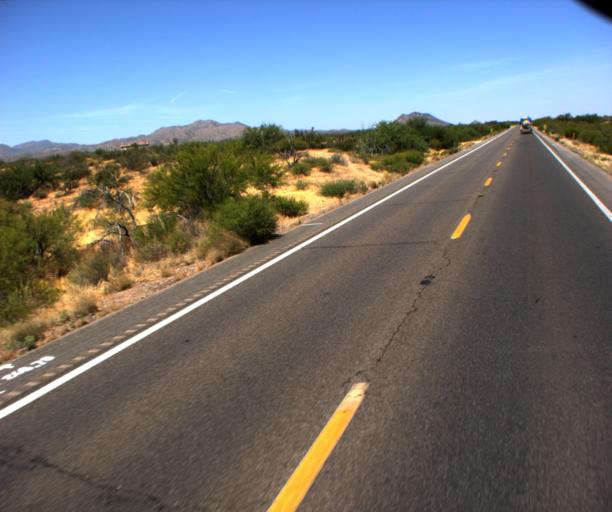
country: US
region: Arizona
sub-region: Gila County
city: Peridot
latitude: 33.3087
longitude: -110.4981
